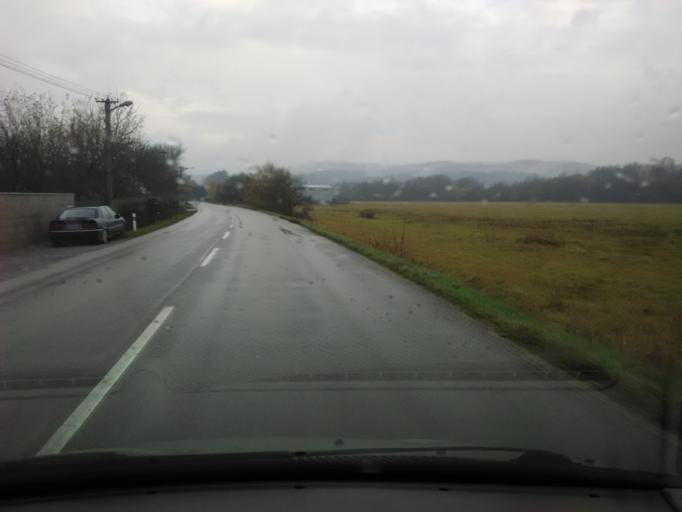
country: SK
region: Zilinsky
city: Bytca
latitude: 49.2180
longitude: 18.5463
